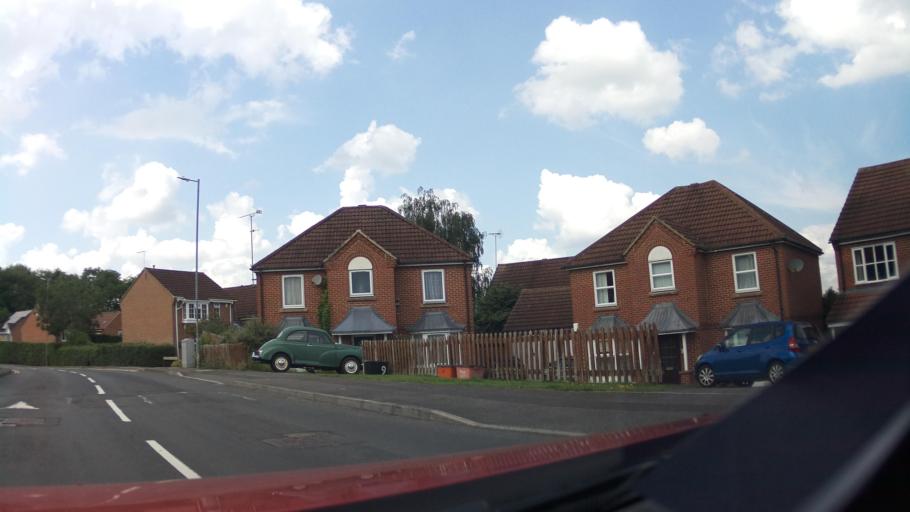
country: GB
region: England
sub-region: Wiltshire
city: Lydiard Tregoze
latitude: 51.5631
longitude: -1.8438
